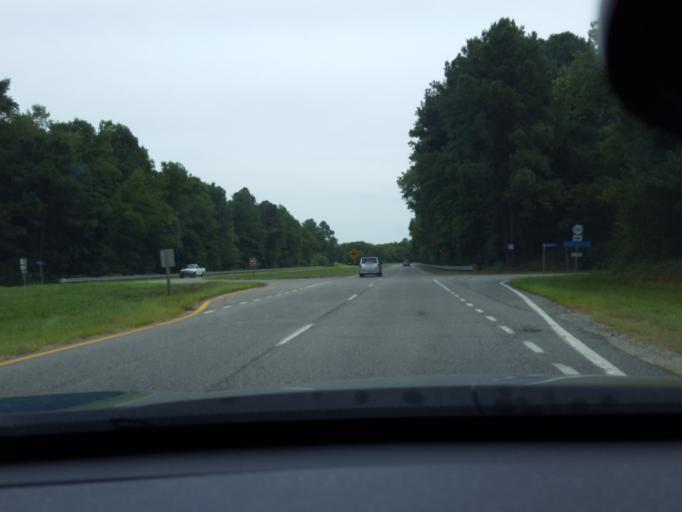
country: US
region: Virginia
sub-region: Caroline County
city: Bowling Green
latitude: 38.0531
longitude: -77.3424
